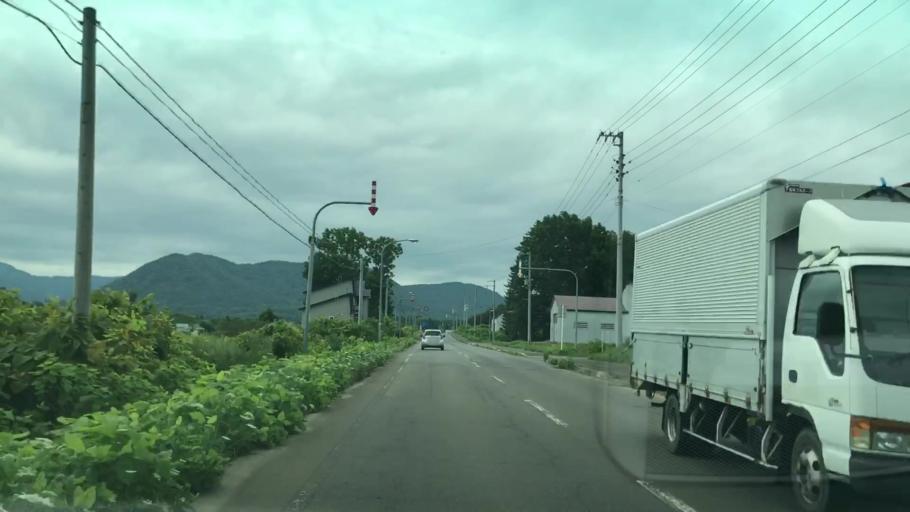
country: JP
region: Hokkaido
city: Yoichi
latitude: 43.0968
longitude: 140.8218
